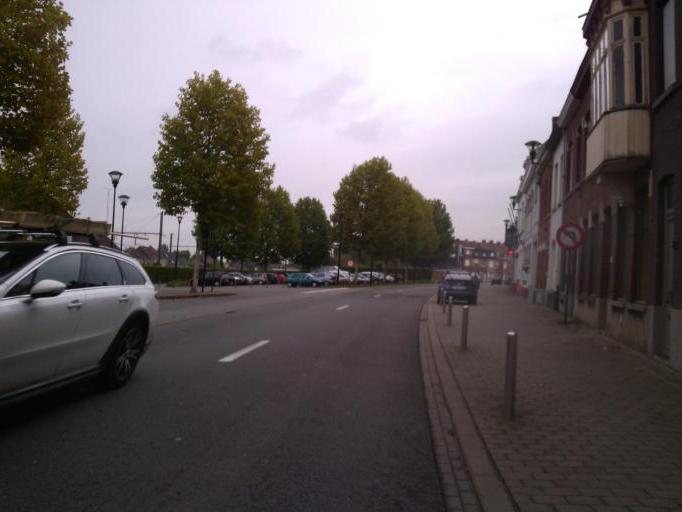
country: BE
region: Flanders
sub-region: Provincie West-Vlaanderen
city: Menen
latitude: 50.7997
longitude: 3.1149
